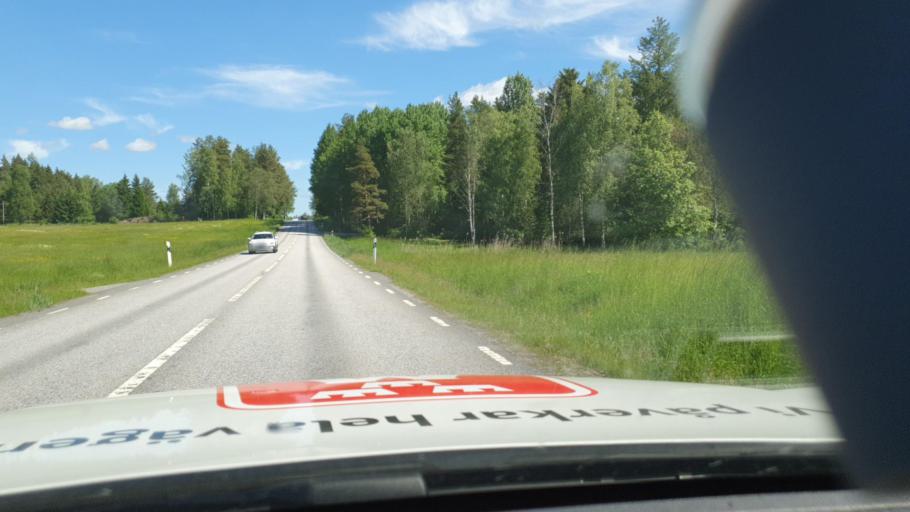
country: SE
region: Stockholm
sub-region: Norrtalje Kommun
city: Rimbo
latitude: 59.6764
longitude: 18.3597
